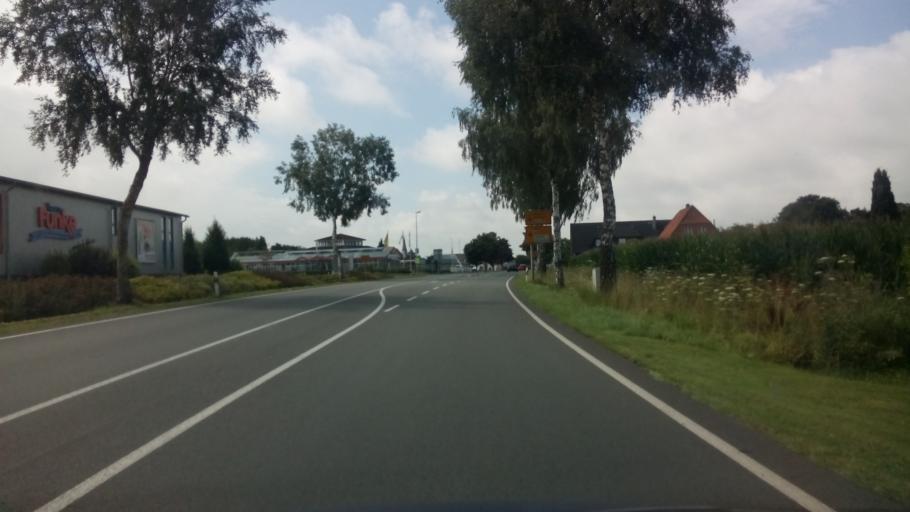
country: DE
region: Lower Saxony
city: Twistringen
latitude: 52.8061
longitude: 8.6511
